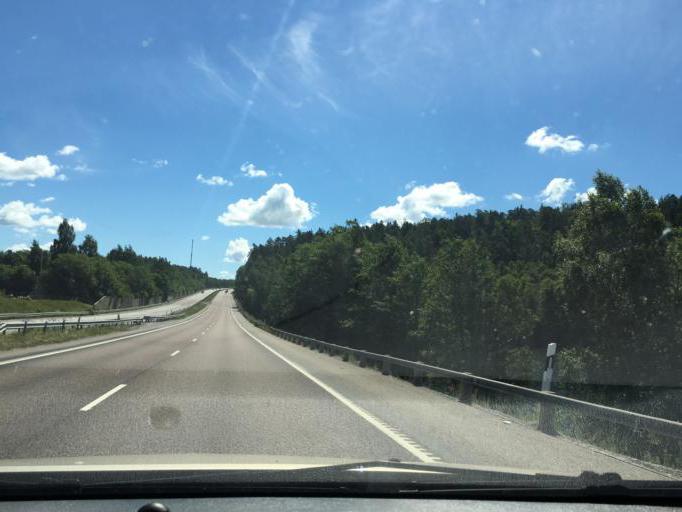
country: SE
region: Stockholm
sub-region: Nacka Kommun
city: Nacka
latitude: 59.3018
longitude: 18.1869
